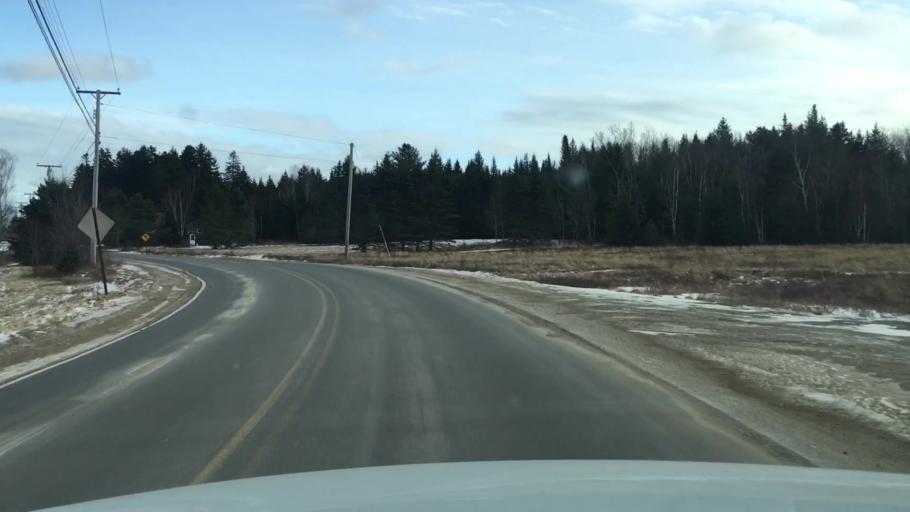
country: US
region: Maine
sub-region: Washington County
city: Jonesport
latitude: 44.6092
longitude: -67.6014
